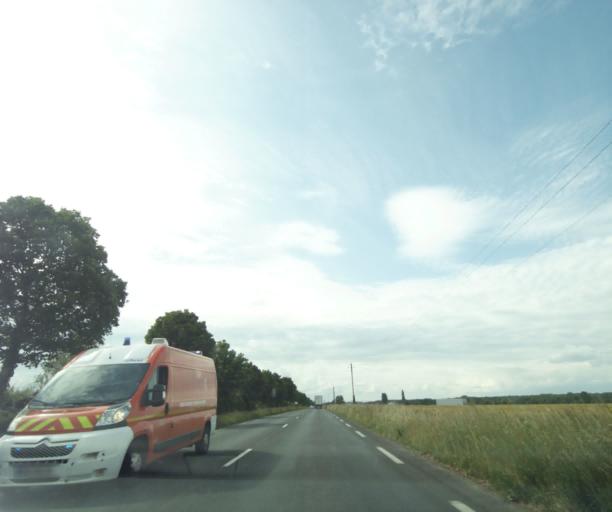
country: FR
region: Pays de la Loire
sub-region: Departement de la Sarthe
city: Solesmes
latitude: 47.8120
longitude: -0.2836
